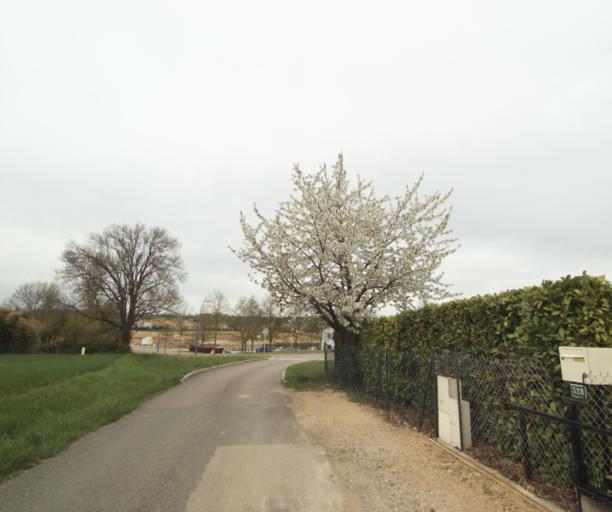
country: FR
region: Bourgogne
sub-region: Departement de Saone-et-Loire
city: Charnay-les-Macon
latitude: 46.3003
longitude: 4.7996
